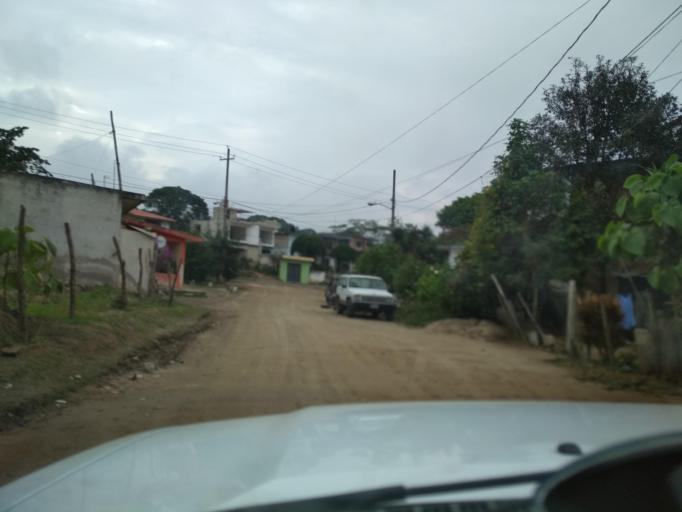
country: MX
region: Veracruz
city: El Castillo
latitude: 19.5631
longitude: -96.8590
